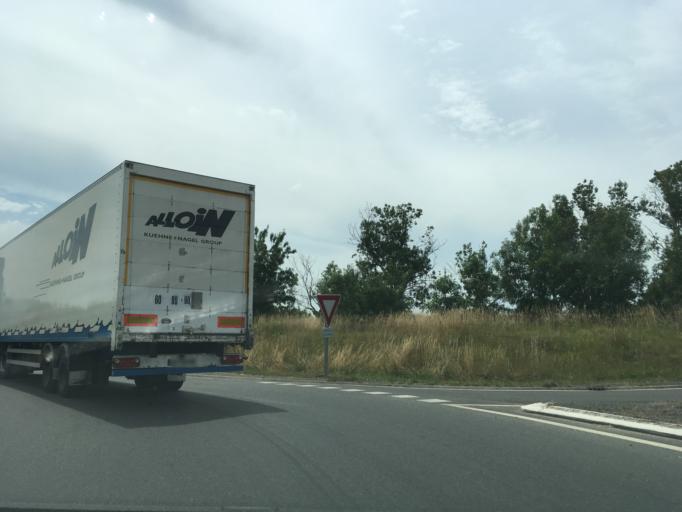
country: FR
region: Poitou-Charentes
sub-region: Departement des Deux-Sevres
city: Niort
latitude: 46.2941
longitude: -0.4670
